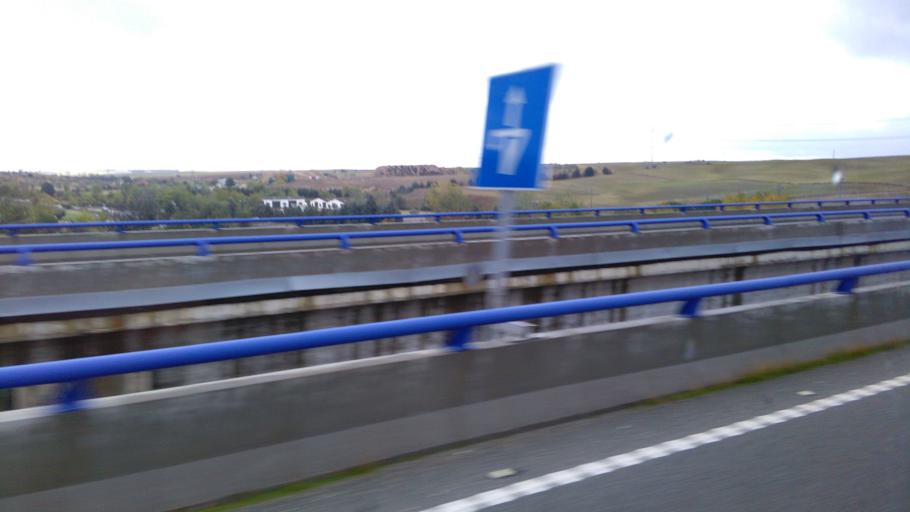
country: ES
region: Madrid
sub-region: Provincia de Madrid
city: Arroyomolinos
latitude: 40.2620
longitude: -3.9045
